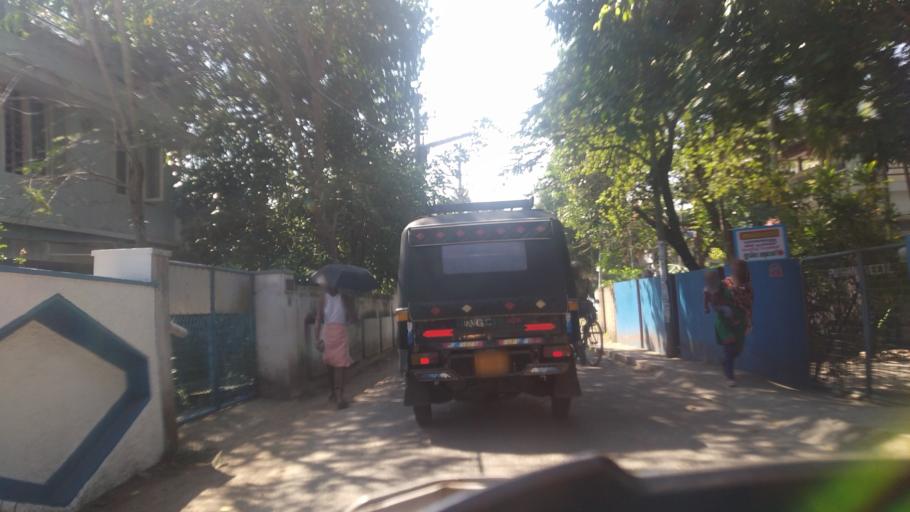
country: IN
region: Kerala
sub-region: Ernakulam
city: Elur
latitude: 10.0361
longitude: 76.2250
